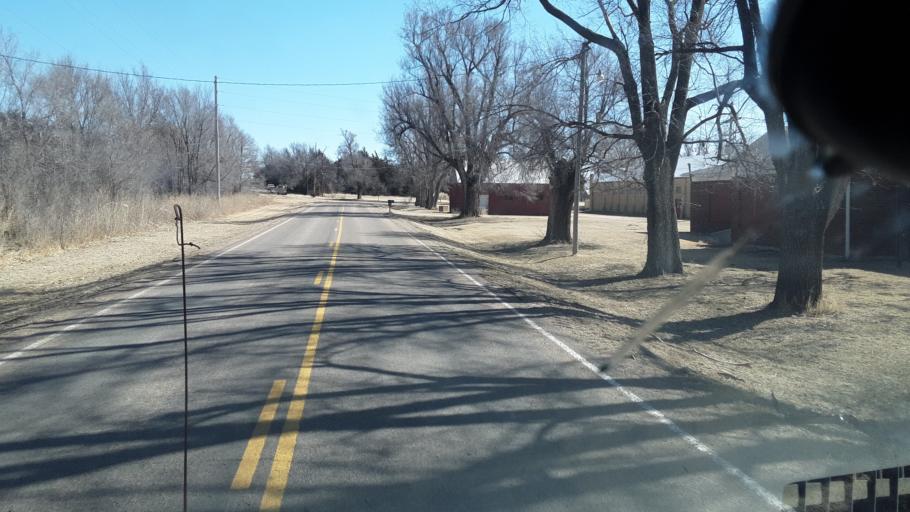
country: US
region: Kansas
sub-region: Barton County
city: Ellinwood
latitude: 38.2820
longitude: -98.4173
